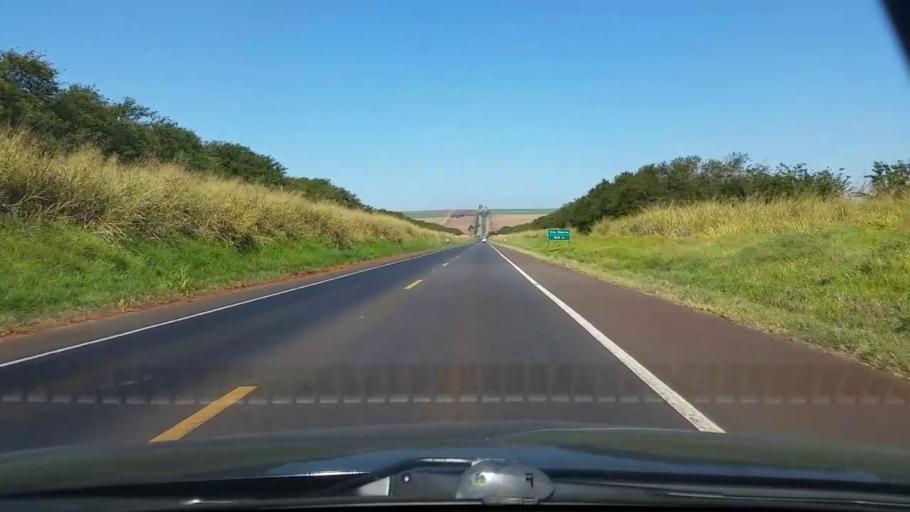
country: BR
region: Sao Paulo
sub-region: Jau
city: Jau
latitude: -22.3624
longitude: -48.5717
